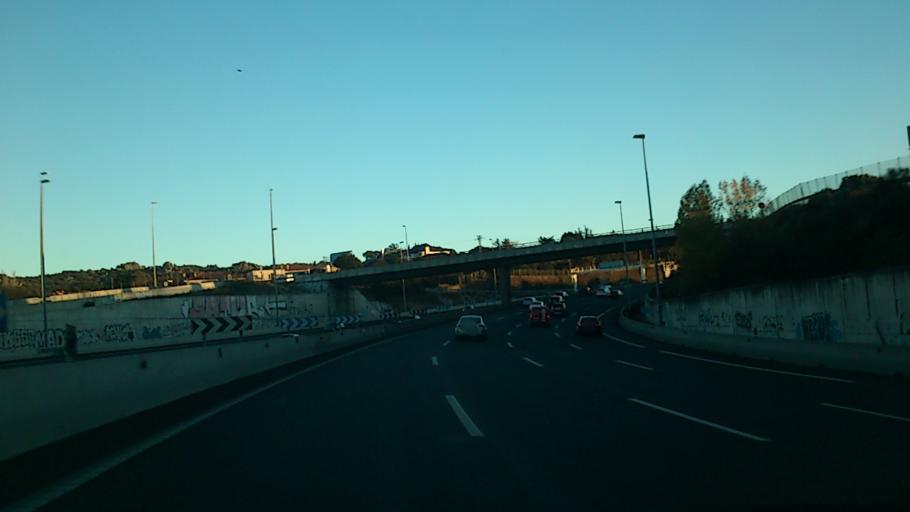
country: ES
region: Madrid
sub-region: Provincia de Madrid
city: Torrelodones
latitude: 40.5960
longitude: -3.9536
